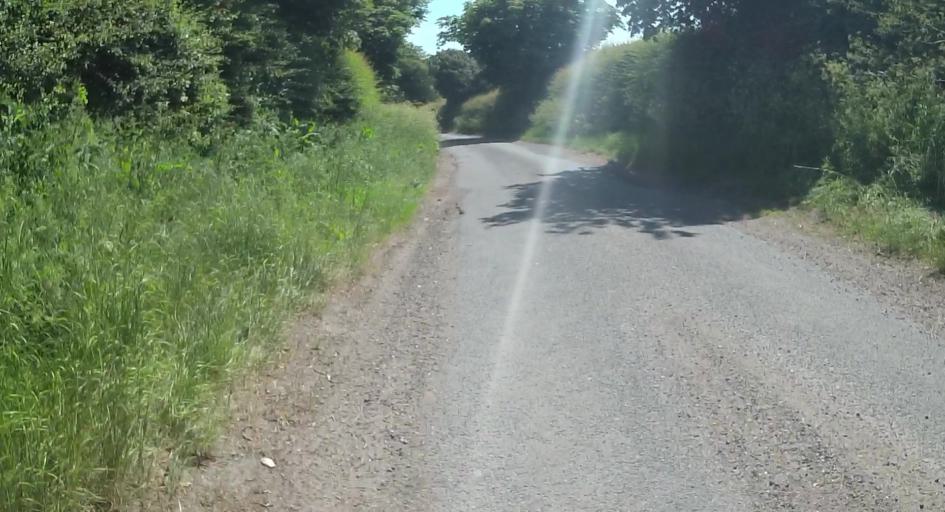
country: GB
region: England
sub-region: Hampshire
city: Kingsclere
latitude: 51.3153
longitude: -1.2954
